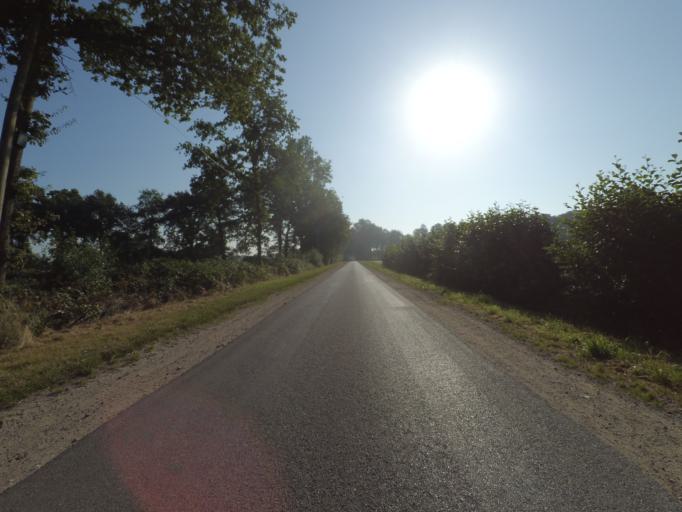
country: DE
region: Lower Saxony
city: Ohne
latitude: 52.2740
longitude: 7.2605
